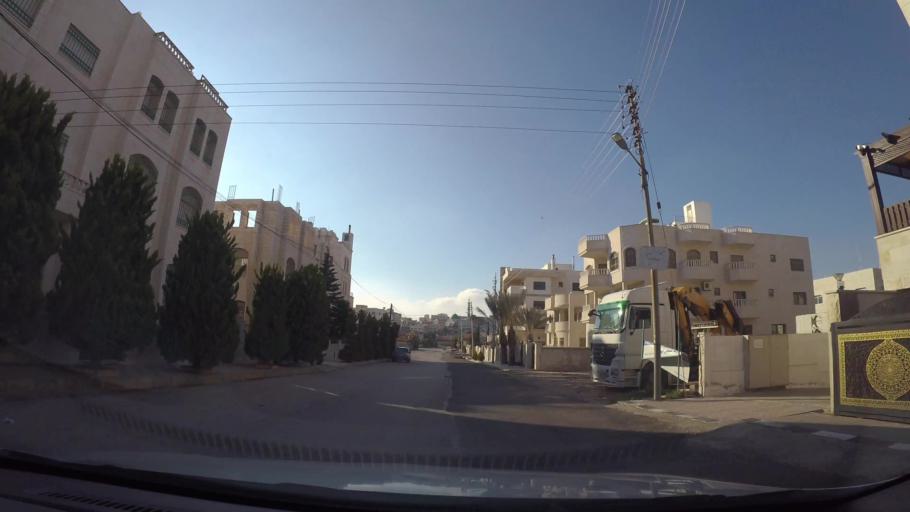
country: JO
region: Amman
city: Al Bunayyat ash Shamaliyah
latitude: 31.9021
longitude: 35.9224
